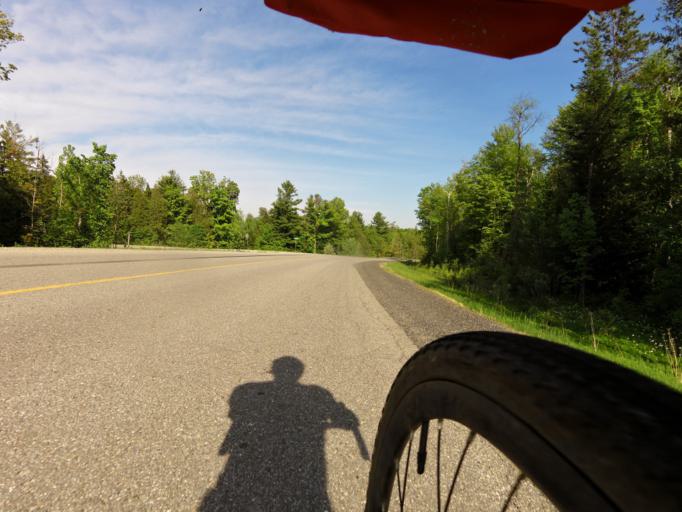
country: CA
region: Ontario
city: Arnprior
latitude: 45.1706
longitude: -76.4908
